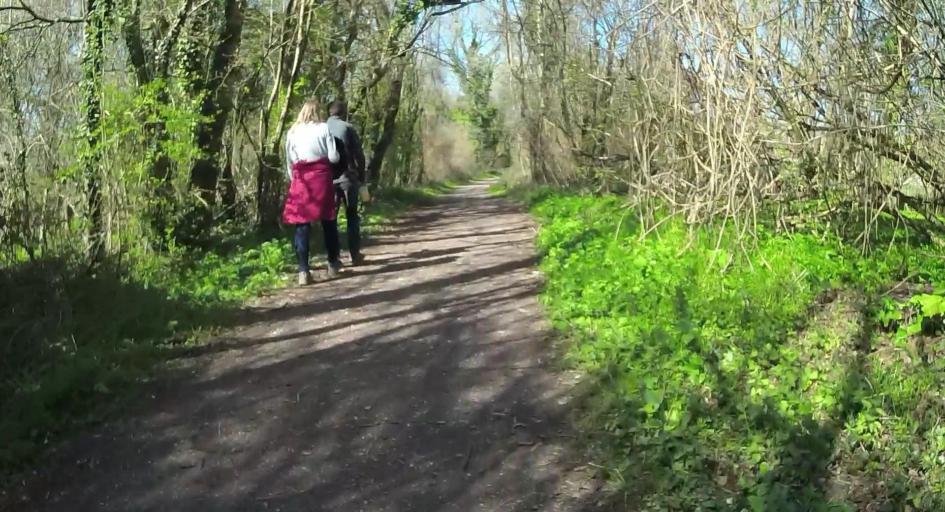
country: GB
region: England
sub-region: Hampshire
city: Abbotts Ann
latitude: 51.0936
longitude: -1.4980
